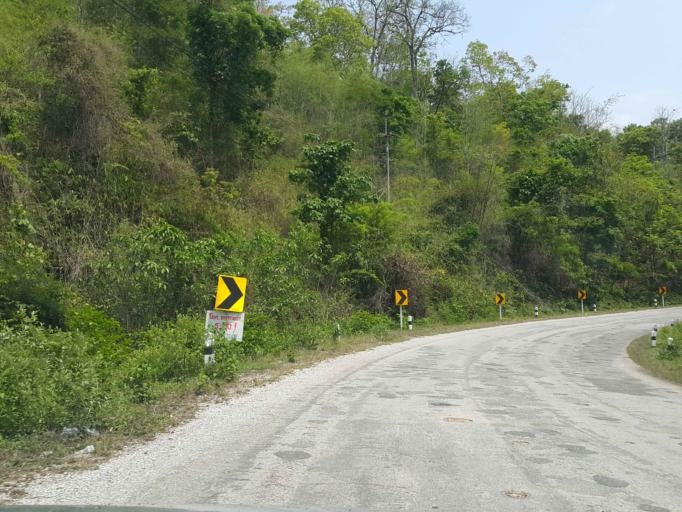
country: TH
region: Lampang
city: Thoen
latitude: 17.6374
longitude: 99.3100
